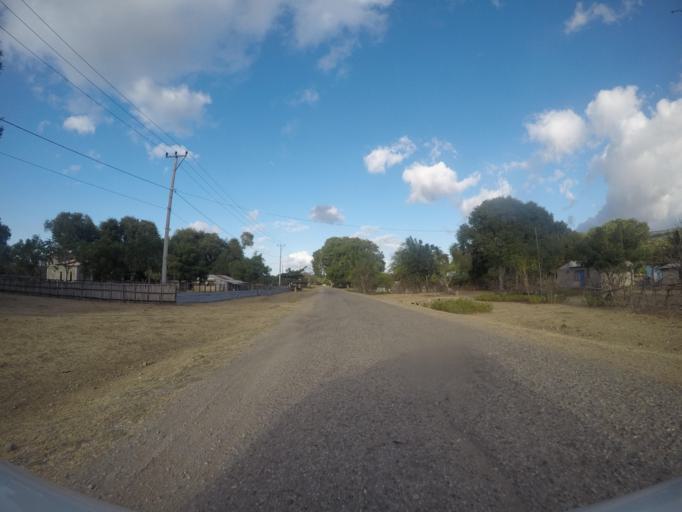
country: TL
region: Lautem
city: Lospalos
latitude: -8.3295
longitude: 126.9743
